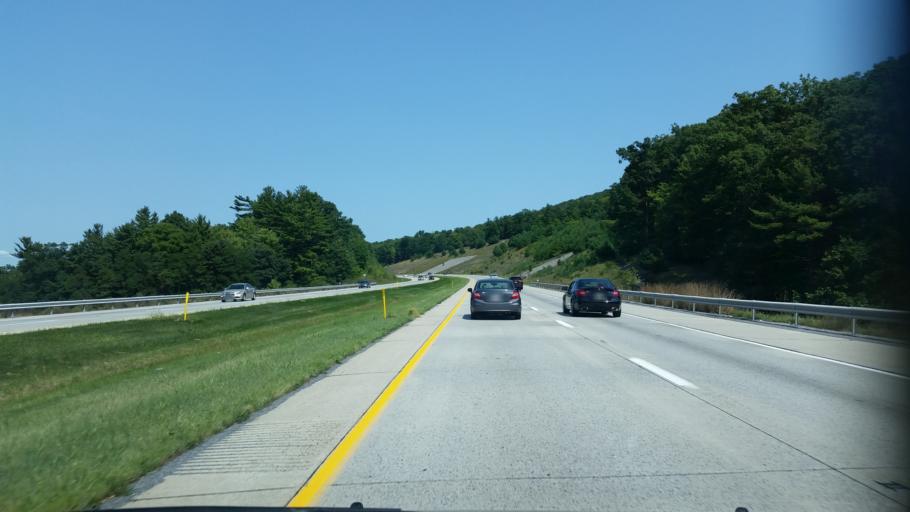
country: US
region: Pennsylvania
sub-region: Blair County
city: Greenwood
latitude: 40.5232
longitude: -78.3574
